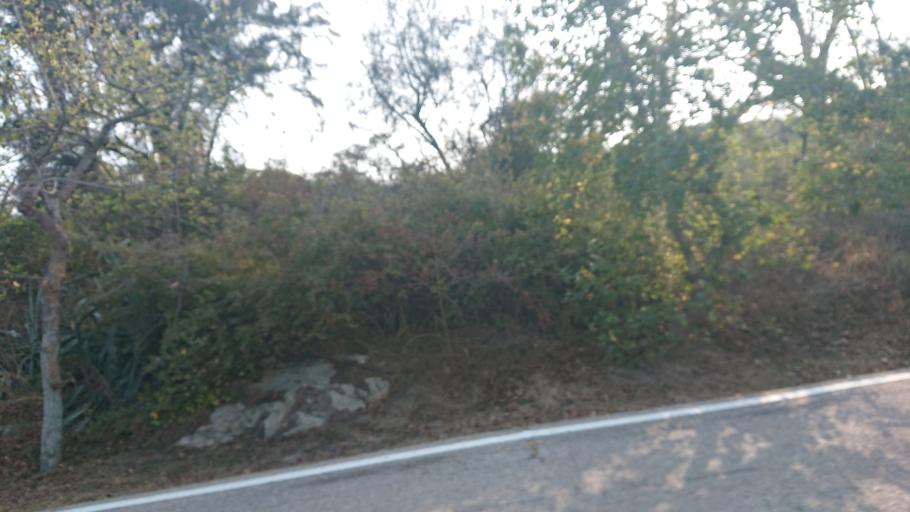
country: CN
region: Fujian
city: Shijing
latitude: 24.5003
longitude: 118.4430
